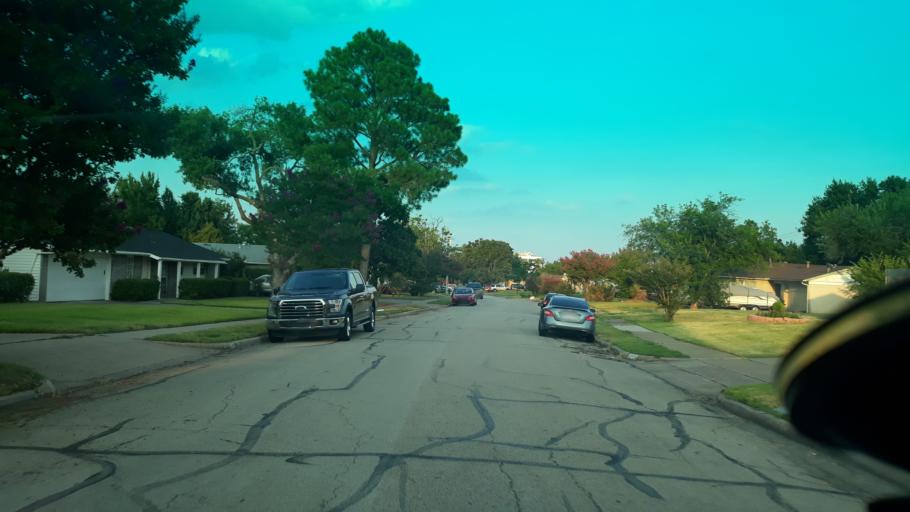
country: US
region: Texas
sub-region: Dallas County
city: Irving
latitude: 32.8396
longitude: -96.9809
